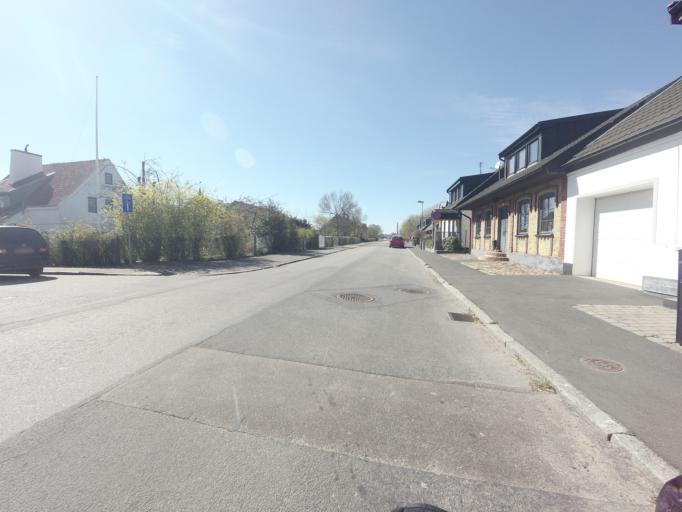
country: SE
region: Skane
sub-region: Trelleborgs Kommun
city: Trelleborg
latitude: 55.3689
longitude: 13.1825
